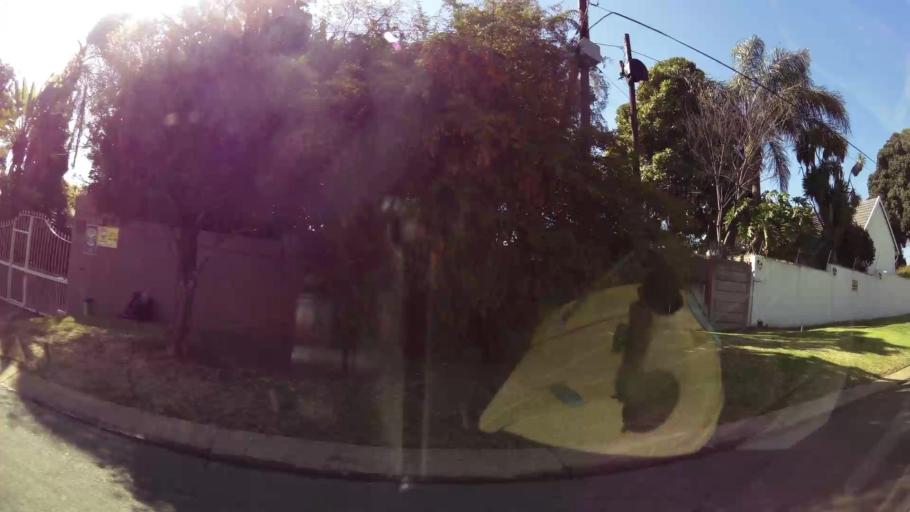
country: ZA
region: Gauteng
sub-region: City of Johannesburg Metropolitan Municipality
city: Modderfontein
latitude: -26.1317
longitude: 28.1077
